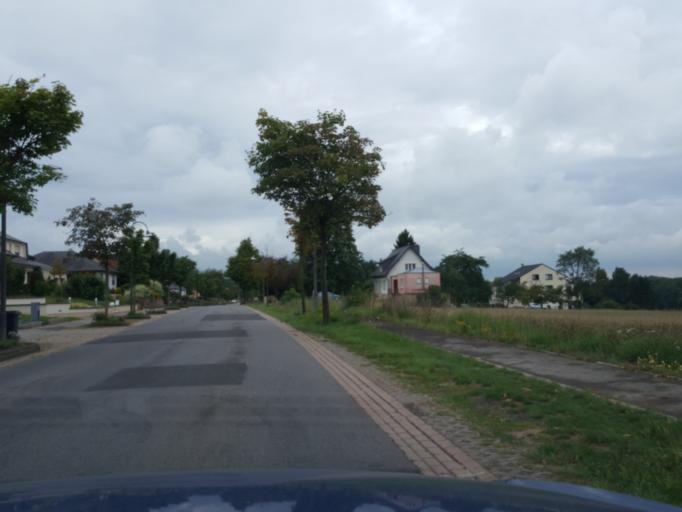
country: LU
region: Luxembourg
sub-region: Canton de Capellen
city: Kopstal
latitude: 49.6888
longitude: 6.0618
